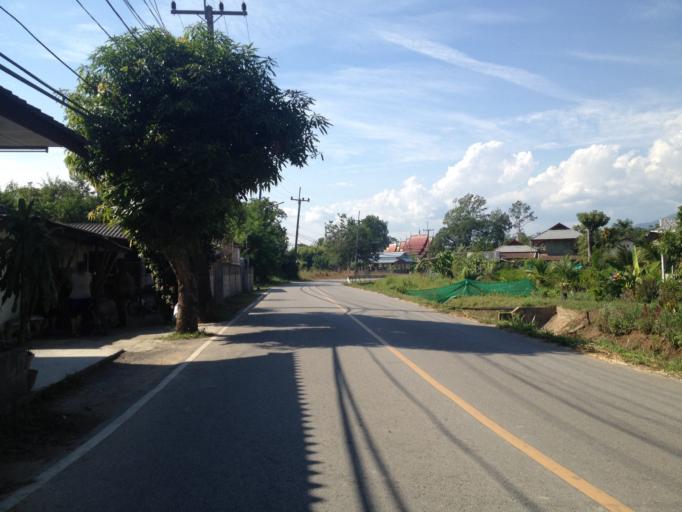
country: TH
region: Chiang Mai
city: Hang Dong
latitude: 18.7240
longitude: 98.9602
